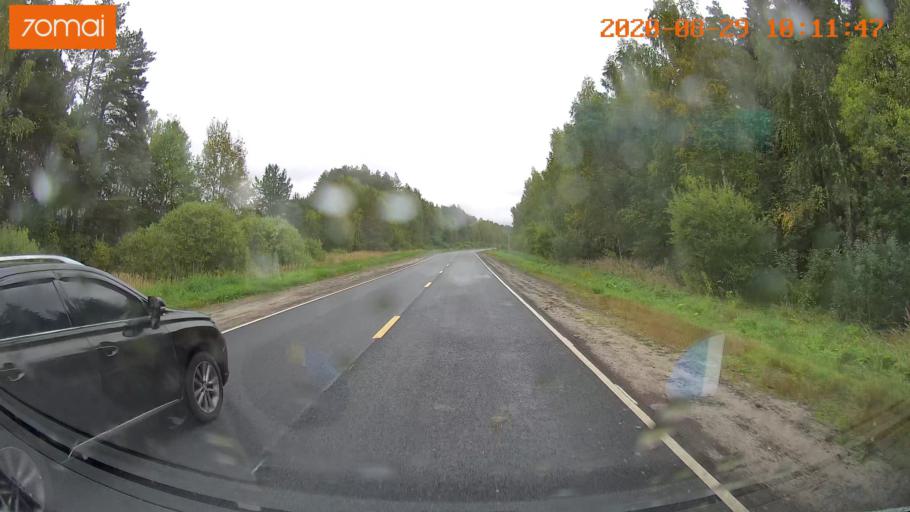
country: RU
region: Ivanovo
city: Kuznechikha
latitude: 57.3746
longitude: 42.6928
